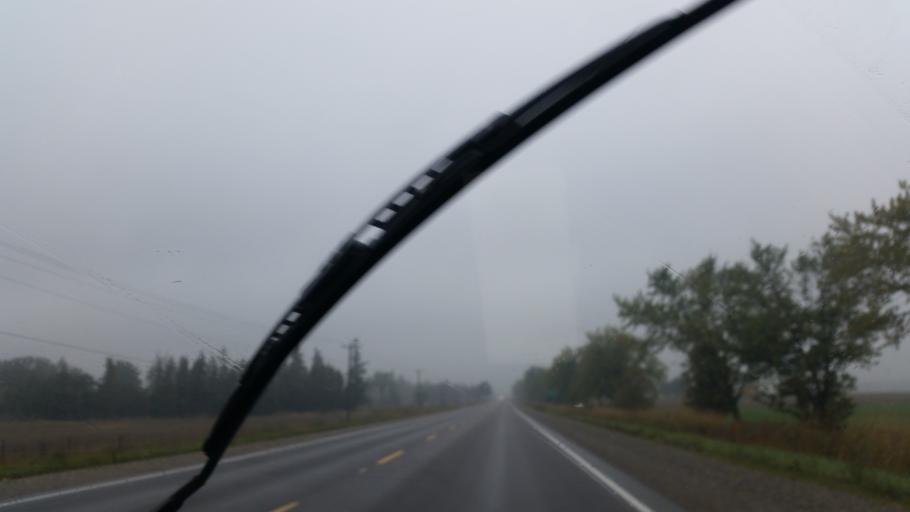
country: CA
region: Ontario
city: Stratford
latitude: 43.2980
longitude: -81.0443
